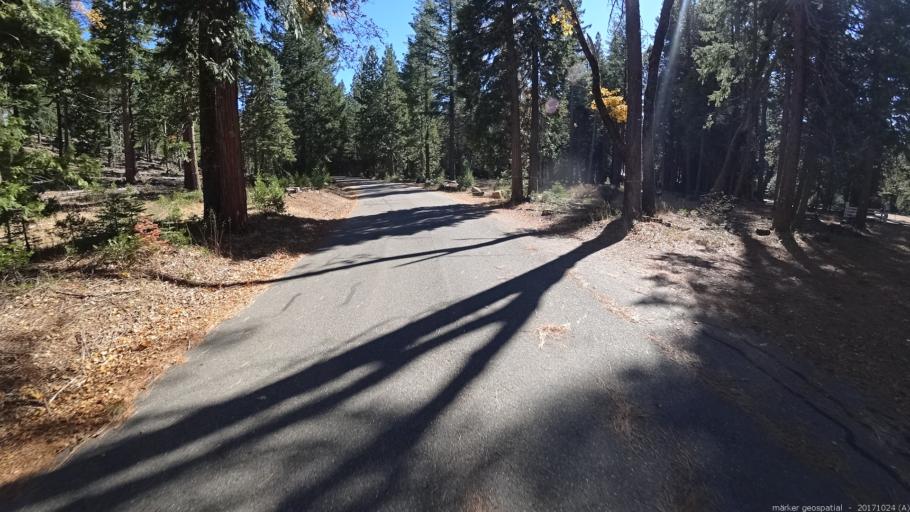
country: US
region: California
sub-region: Shasta County
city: Shingletown
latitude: 40.5032
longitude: -121.6622
